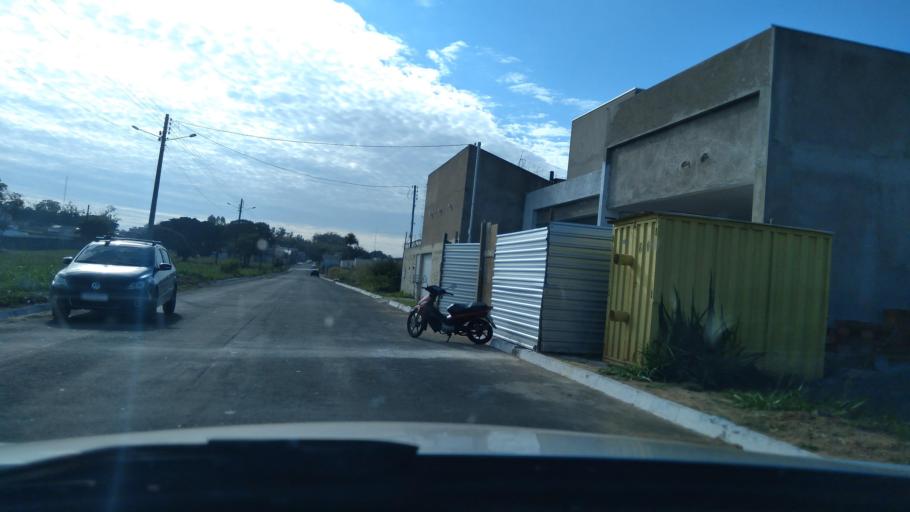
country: BR
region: Goias
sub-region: Mineiros
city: Mineiros
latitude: -17.5555
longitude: -52.5617
